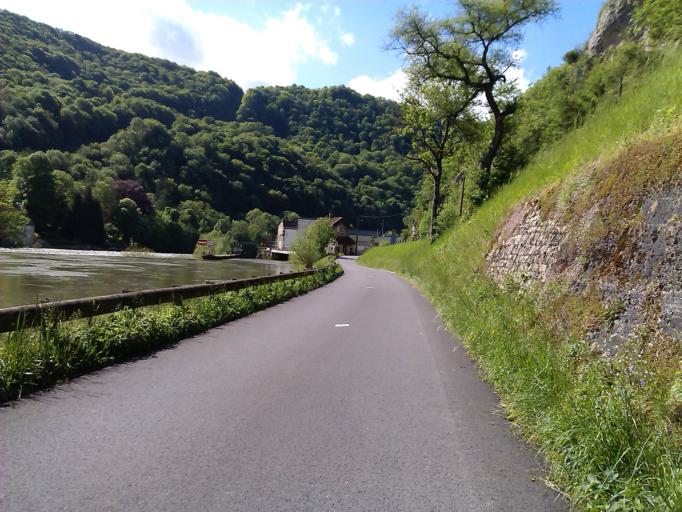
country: FR
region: Franche-Comte
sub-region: Departement du Doubs
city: Roulans
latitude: 47.3024
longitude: 6.2352
